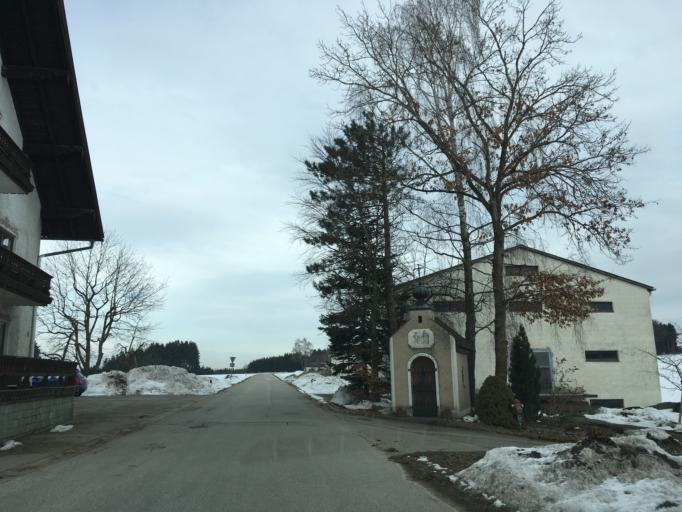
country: DE
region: Bavaria
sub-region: Upper Bavaria
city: Unterreit
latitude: 48.1126
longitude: 12.3785
